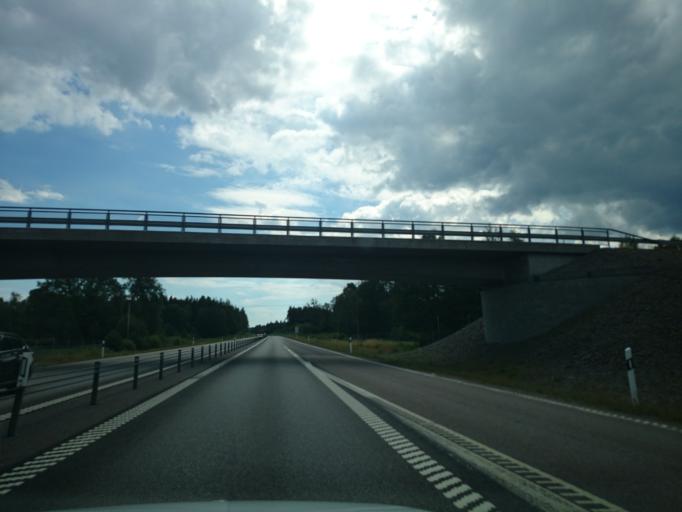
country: SE
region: Kalmar
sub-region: Kalmar Kommun
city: Ljungbyholm
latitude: 56.5513
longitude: 16.0855
